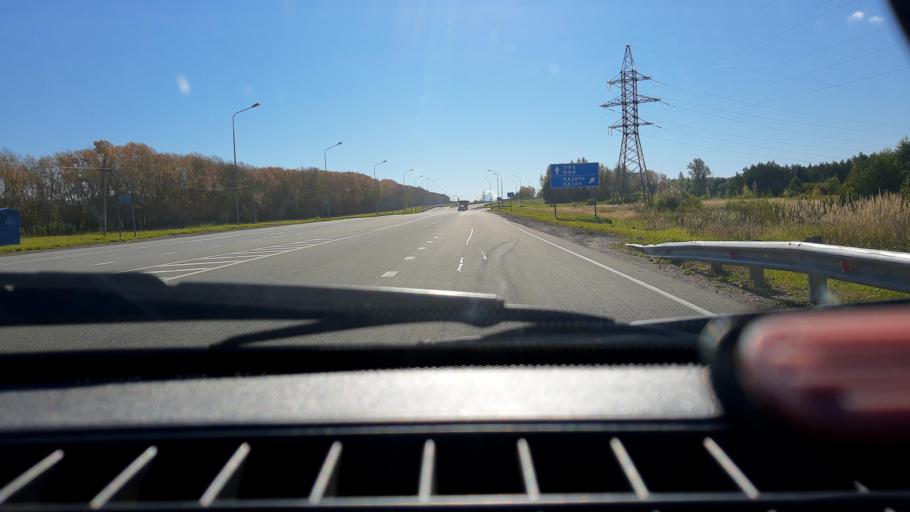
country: RU
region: Bashkortostan
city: Kushnarenkovo
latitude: 55.0637
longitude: 55.4219
